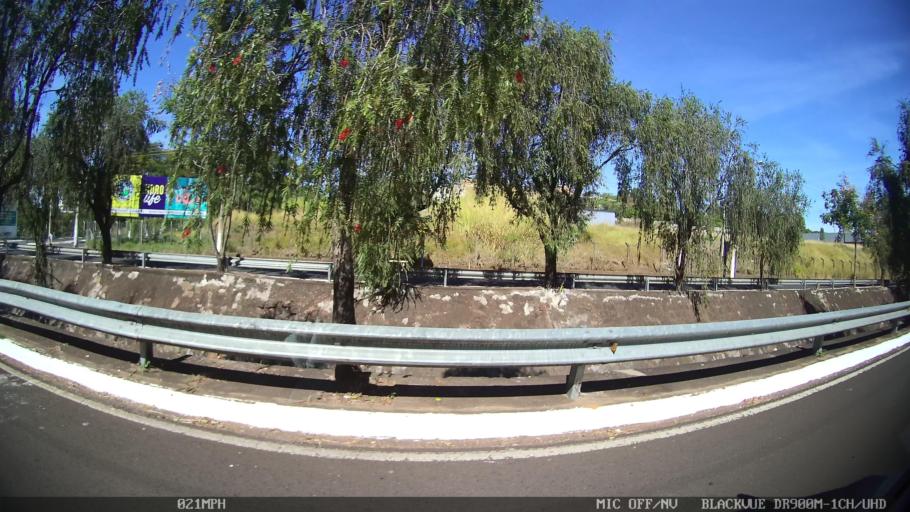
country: BR
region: Sao Paulo
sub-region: Franca
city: Franca
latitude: -20.5362
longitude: -47.3800
